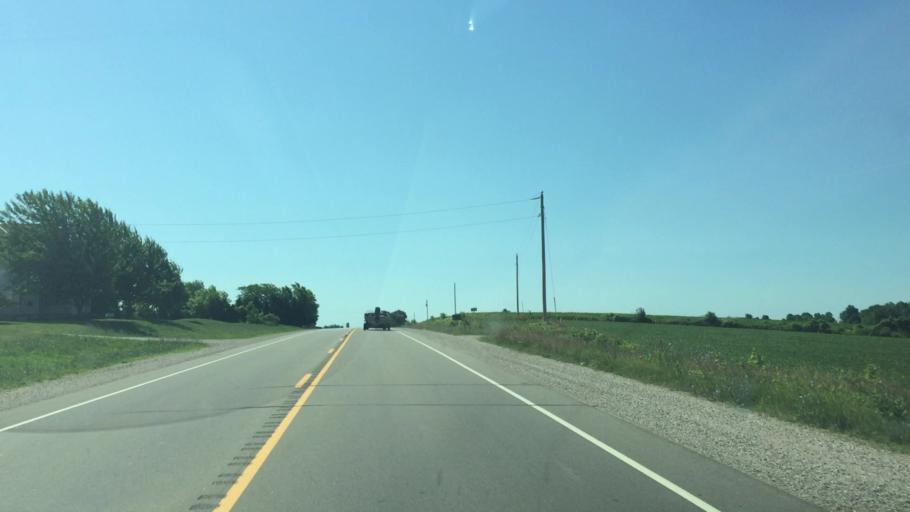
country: US
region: Wisconsin
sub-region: Calumet County
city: Chilton
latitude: 44.0138
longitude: -88.1466
